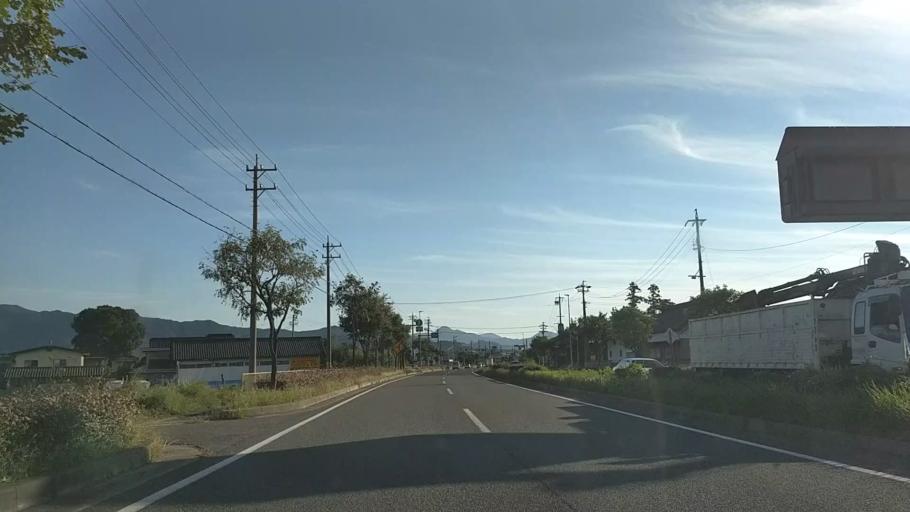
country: JP
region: Nagano
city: Nagano-shi
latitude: 36.6004
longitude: 138.1934
